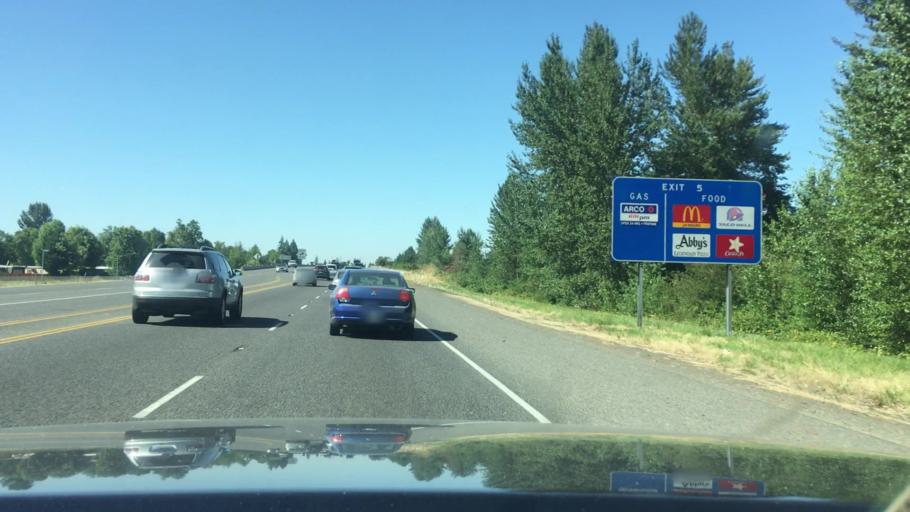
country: US
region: Oregon
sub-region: Lane County
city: Eugene
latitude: 44.0654
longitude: -123.1736
